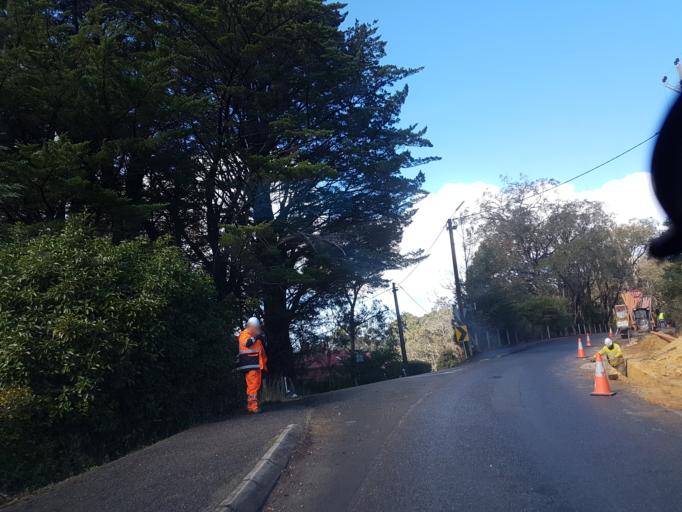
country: AU
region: South Australia
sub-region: Adelaide Hills
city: Heathfield
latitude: -35.0119
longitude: 138.7107
